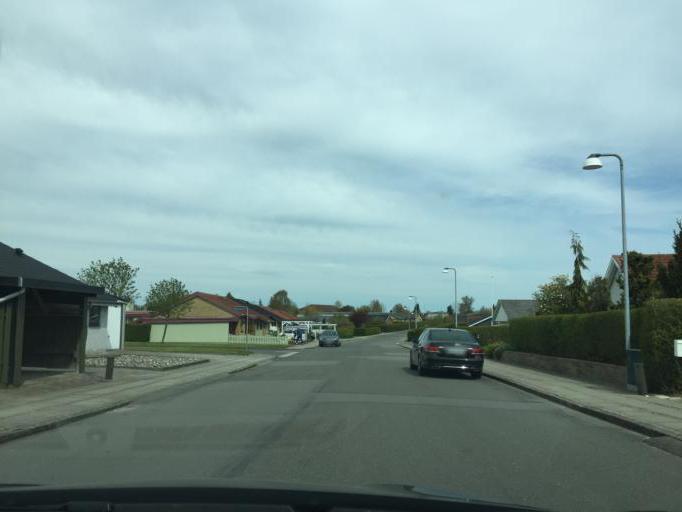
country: DK
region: South Denmark
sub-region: Odense Kommune
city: Odense
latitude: 55.4076
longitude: 10.3283
